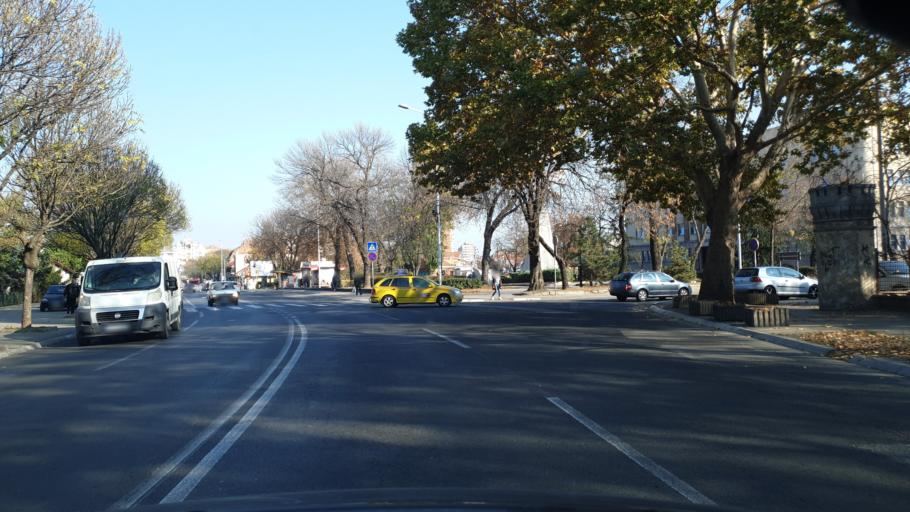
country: RS
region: Central Serbia
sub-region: Nisavski Okrug
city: Nis
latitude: 43.3157
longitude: 21.8820
